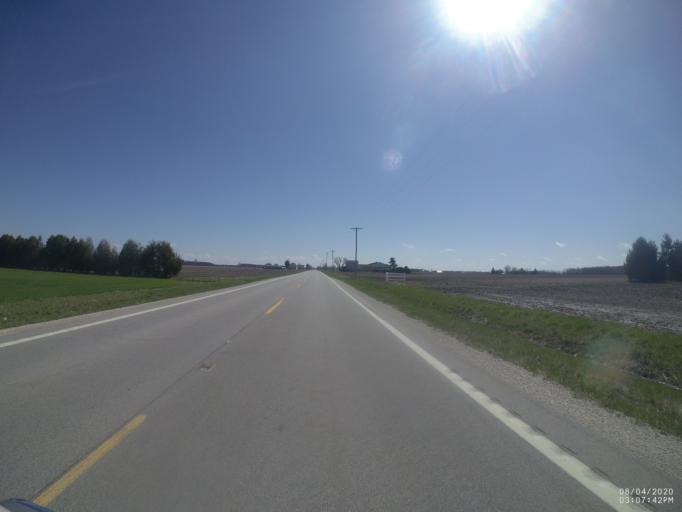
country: US
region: Ohio
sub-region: Sandusky County
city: Stony Prairie
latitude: 41.2937
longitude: -83.2358
